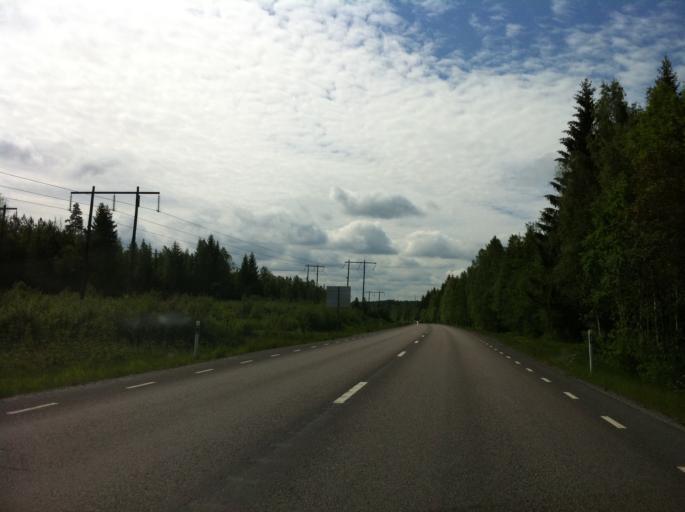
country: SE
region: Vaermland
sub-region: Karlstads Kommun
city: Edsvalla
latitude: 59.4162
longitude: 13.1861
